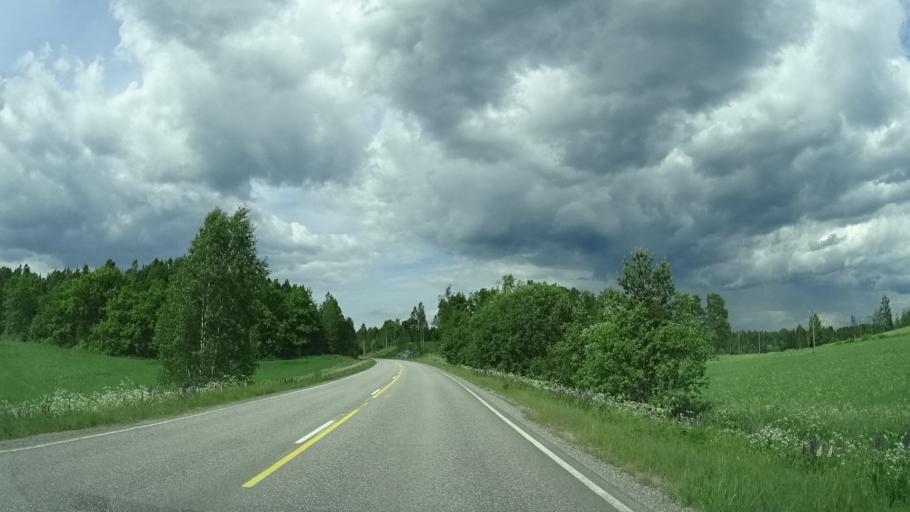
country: FI
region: Uusimaa
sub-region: Helsinki
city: Siuntio
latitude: 60.1874
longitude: 24.2037
